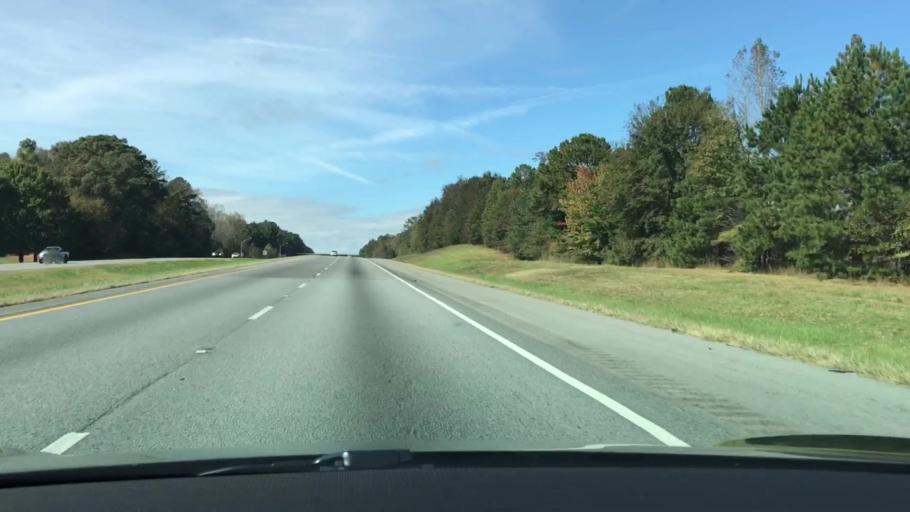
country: US
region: Georgia
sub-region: Walton County
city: Social Circle
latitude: 33.6034
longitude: -83.6608
